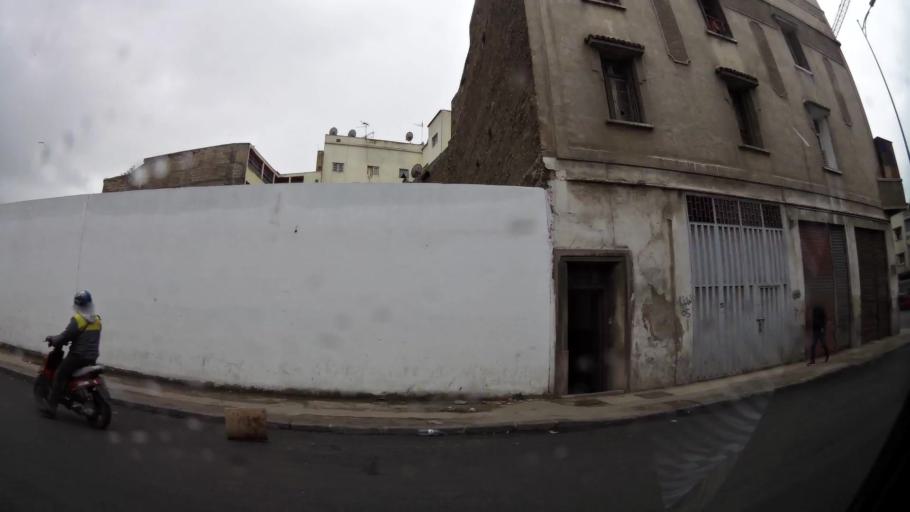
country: MA
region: Grand Casablanca
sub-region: Casablanca
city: Casablanca
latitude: 33.5773
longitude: -7.5971
